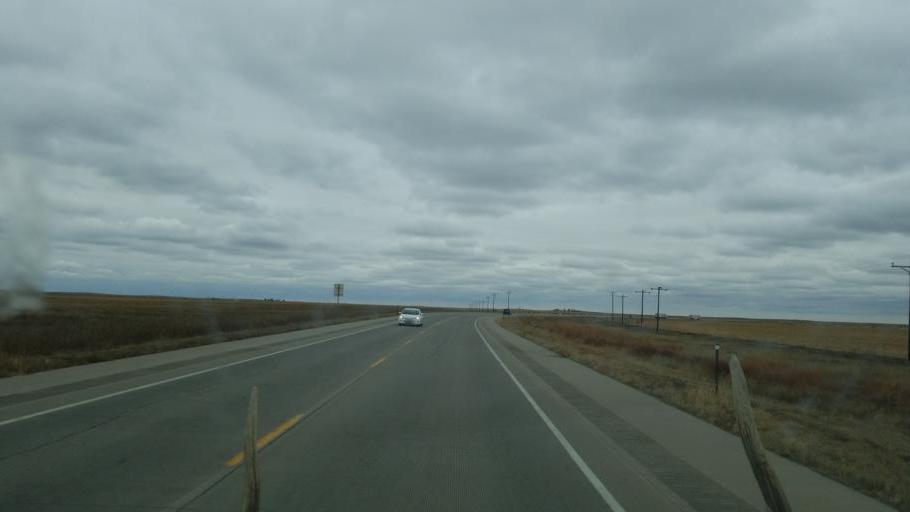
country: US
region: Colorado
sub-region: Kiowa County
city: Eads
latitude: 38.6761
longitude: -102.7859
